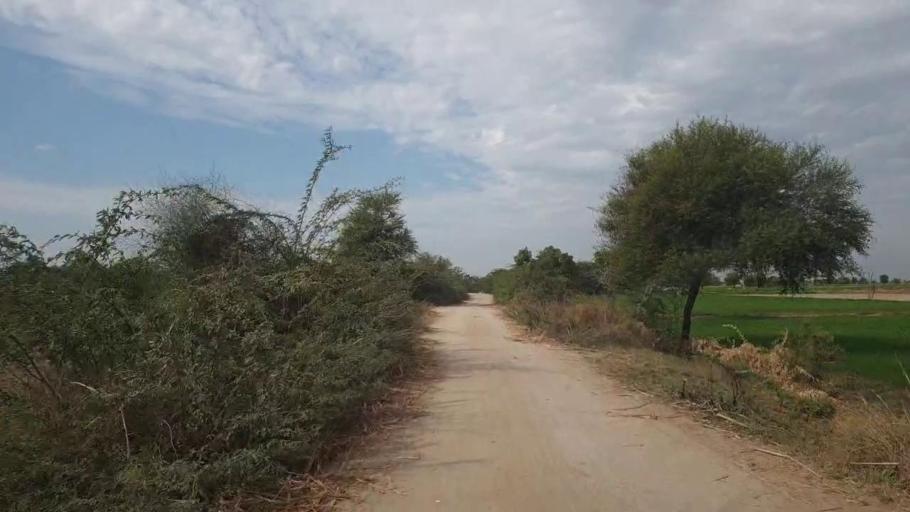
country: PK
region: Sindh
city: Jhol
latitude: 26.0109
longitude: 68.8691
